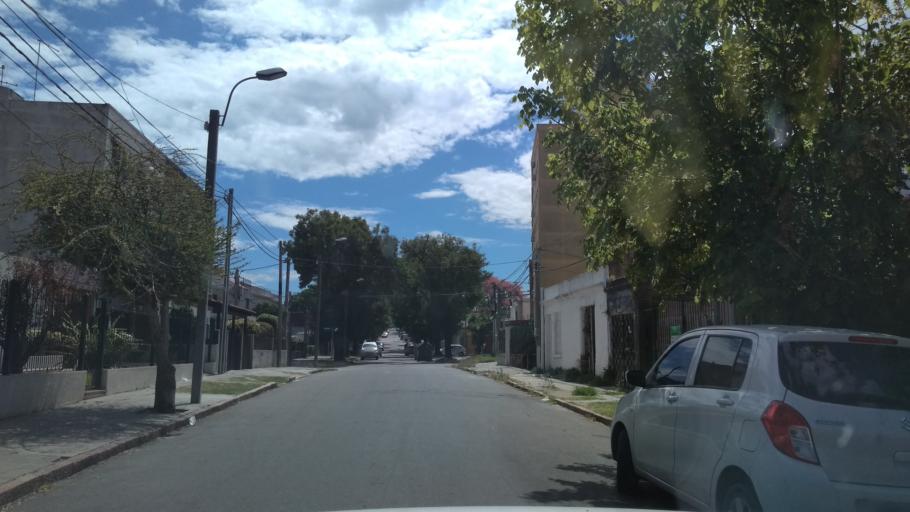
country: UY
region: Montevideo
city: Montevideo
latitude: -34.8930
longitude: -56.1211
